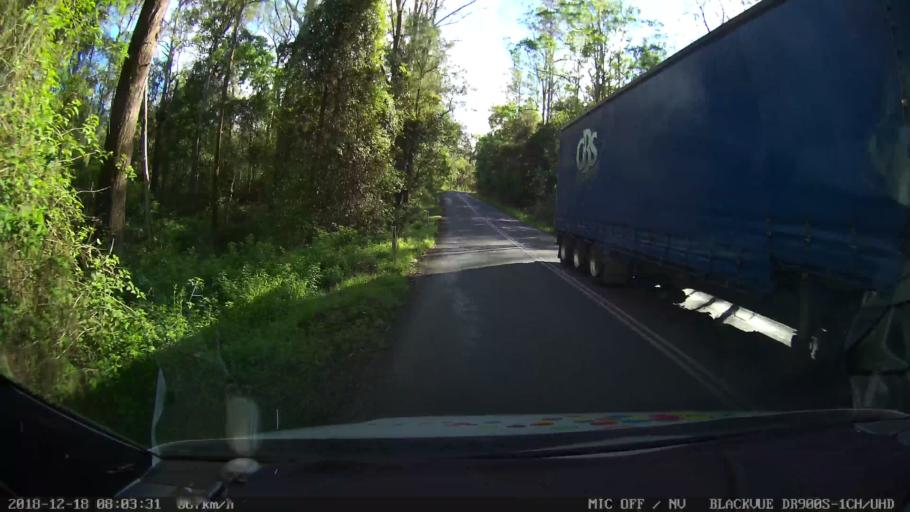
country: AU
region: New South Wales
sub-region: Kyogle
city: Kyogle
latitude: -28.3851
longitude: 152.6414
